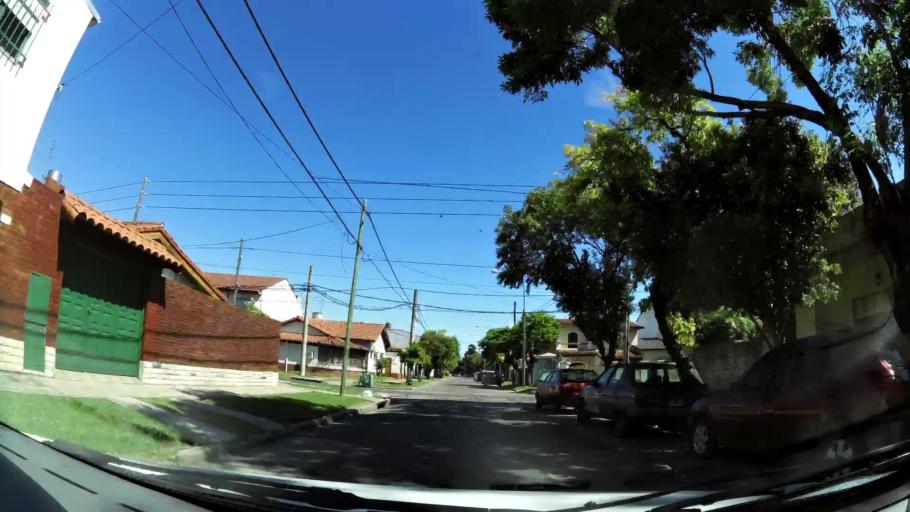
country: AR
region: Buenos Aires
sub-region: Partido de General San Martin
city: General San Martin
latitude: -34.5238
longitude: -58.5349
